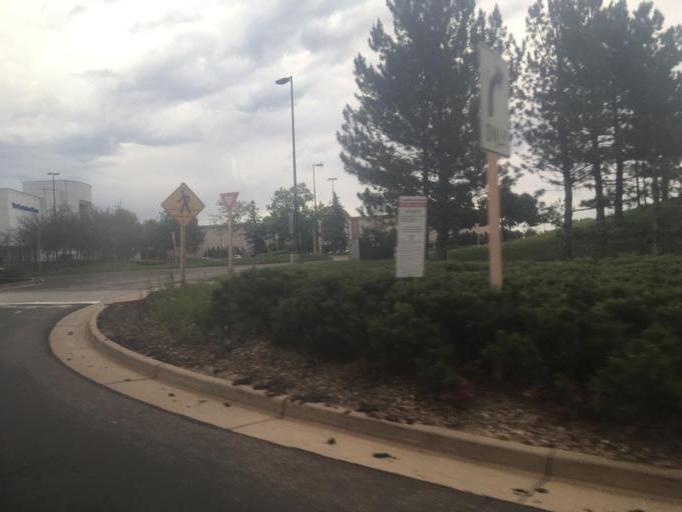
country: US
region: Colorado
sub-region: Boulder County
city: Superior
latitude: 39.9302
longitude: -105.1313
